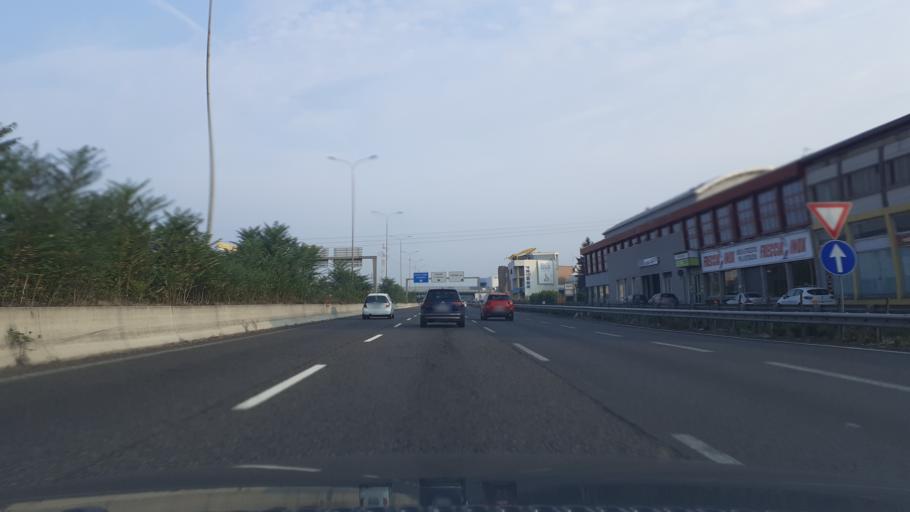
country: IT
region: Lombardy
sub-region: Provincia di Monza e Brianza
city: Santa Margherita
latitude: 45.6319
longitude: 9.2250
